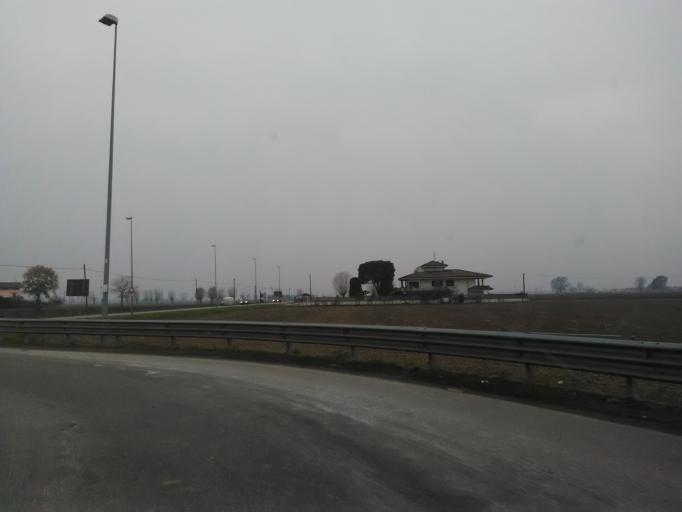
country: IT
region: Piedmont
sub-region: Provincia di Vercelli
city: Tronzano Vercellese
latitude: 45.3413
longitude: 8.1617
